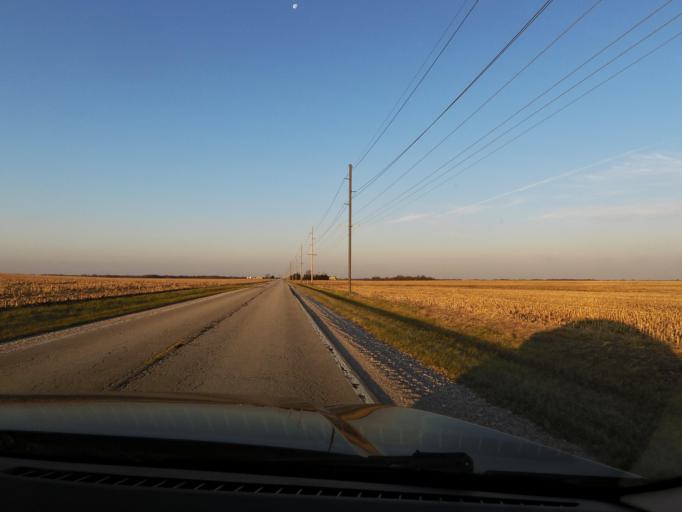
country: US
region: Illinois
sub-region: Marion County
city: Odin
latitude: 38.7651
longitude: -89.0167
